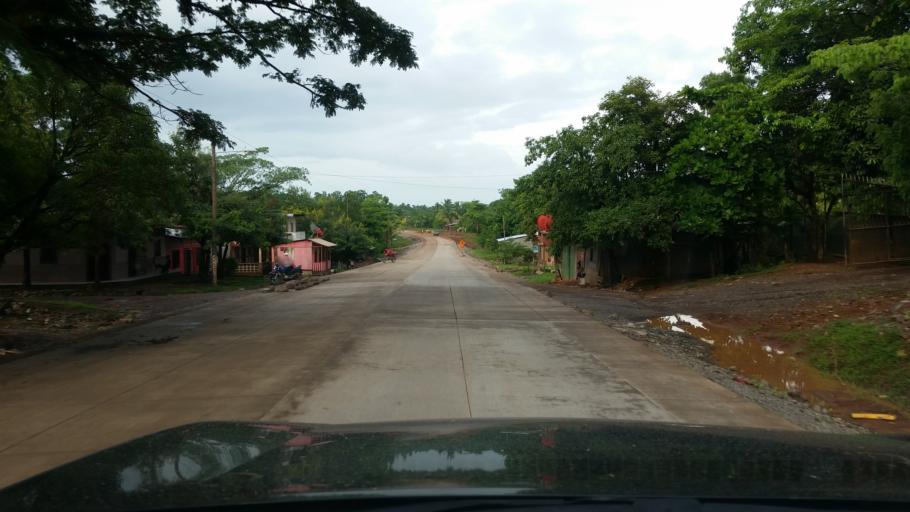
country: NI
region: Matagalpa
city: Rio Blanco
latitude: 13.1202
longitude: -85.0575
